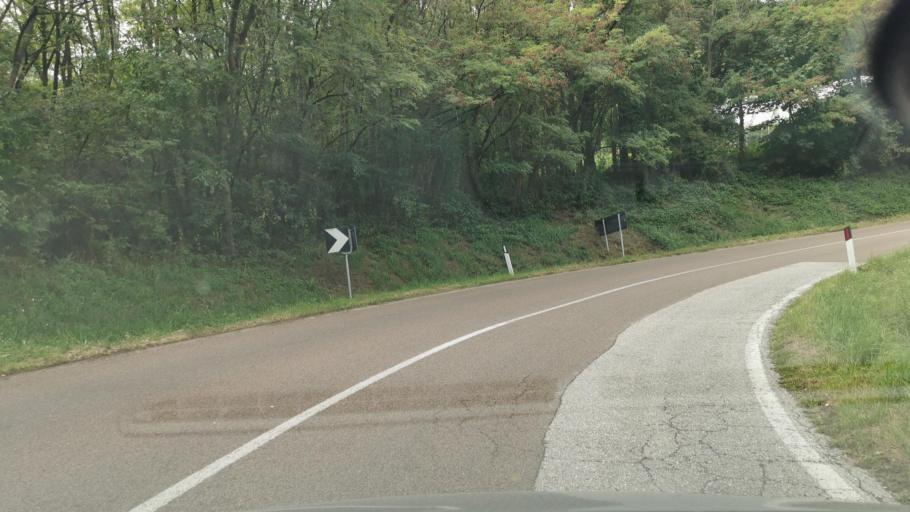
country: IT
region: Trentino-Alto Adige
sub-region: Provincia di Trento
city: Frassilongo
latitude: 46.0830
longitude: 11.2762
